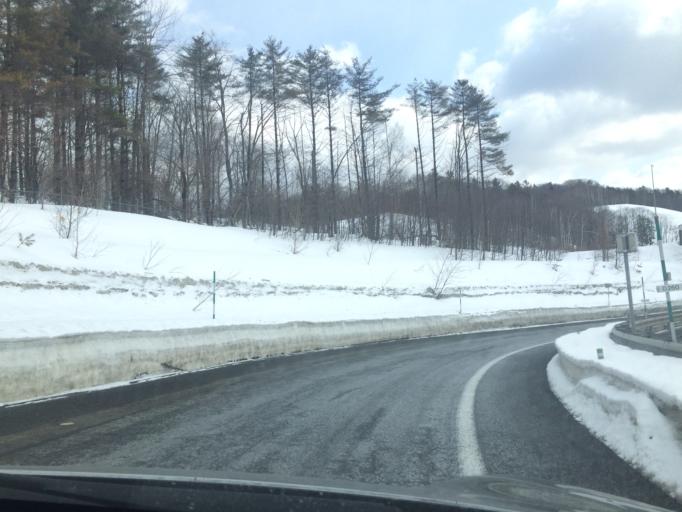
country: JP
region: Hokkaido
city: Shimo-furano
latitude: 42.9799
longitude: 142.4080
